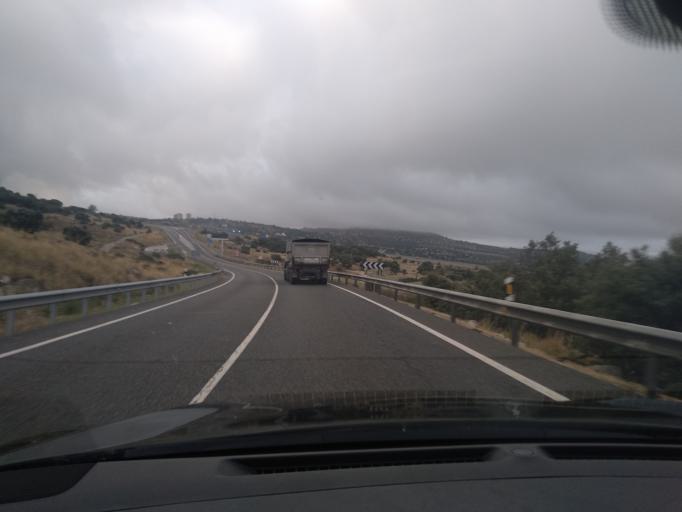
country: ES
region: Castille and Leon
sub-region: Provincia de Segovia
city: Otero de Herreros
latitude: 40.7949
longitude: -4.2165
